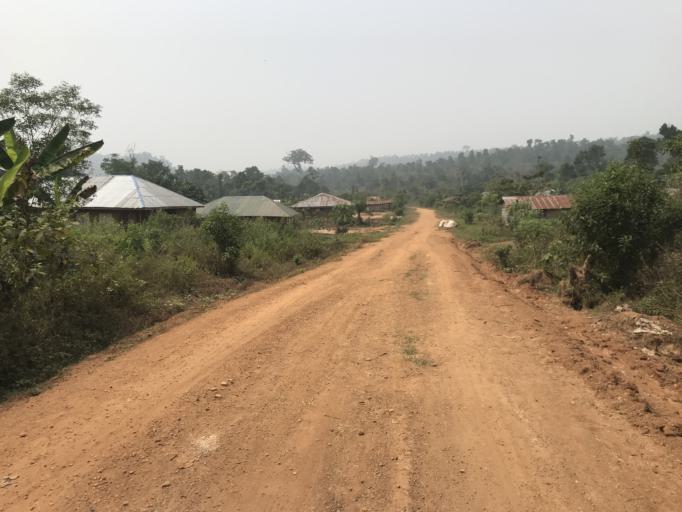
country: NG
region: Osun
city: Ifetedo
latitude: 7.0262
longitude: 4.4747
